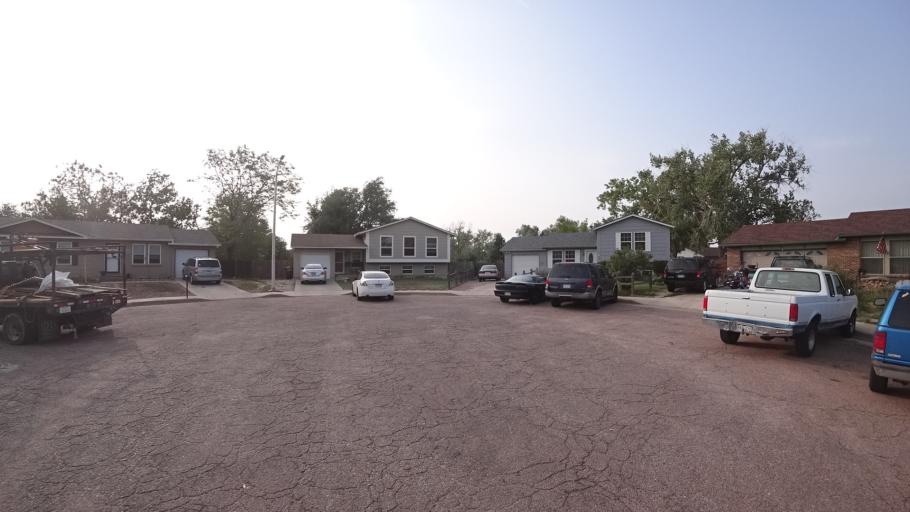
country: US
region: Colorado
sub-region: El Paso County
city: Stratmoor
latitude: 38.7985
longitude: -104.7528
